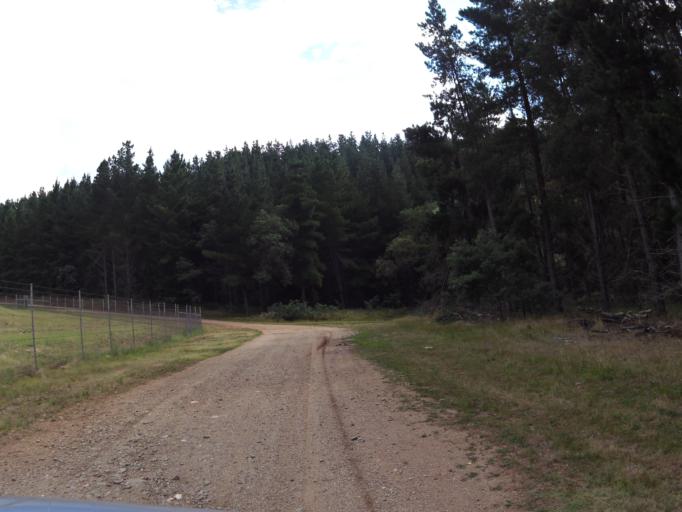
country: AU
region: Victoria
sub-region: Alpine
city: Mount Beauty
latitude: -36.7623
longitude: 147.0203
